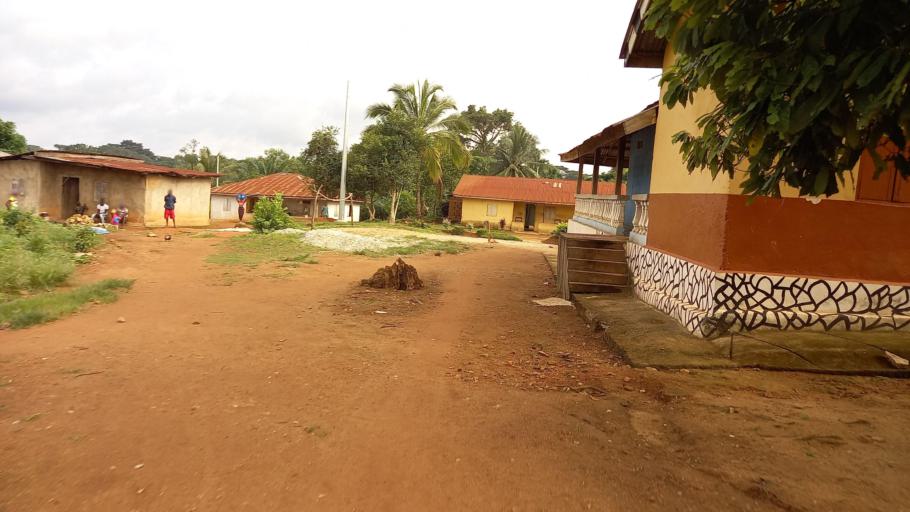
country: SL
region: Eastern Province
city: Kailahun
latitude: 8.2764
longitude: -10.5786
